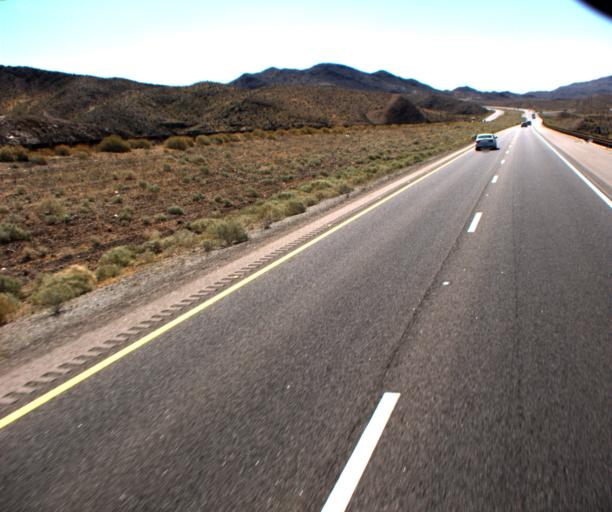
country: US
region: Nevada
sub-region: Clark County
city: Boulder City
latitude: 35.8704
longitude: -114.6079
